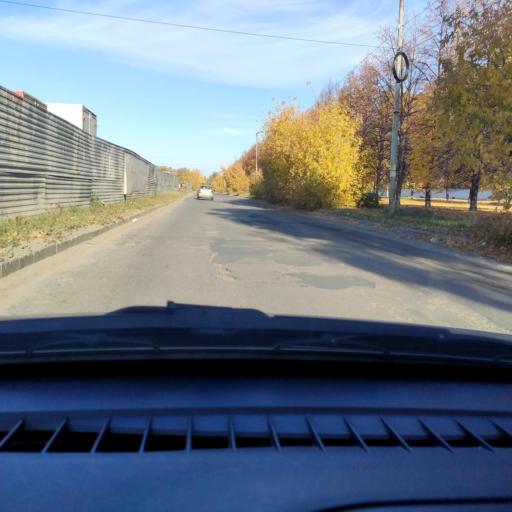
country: RU
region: Samara
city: Tol'yatti
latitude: 53.5381
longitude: 49.3065
